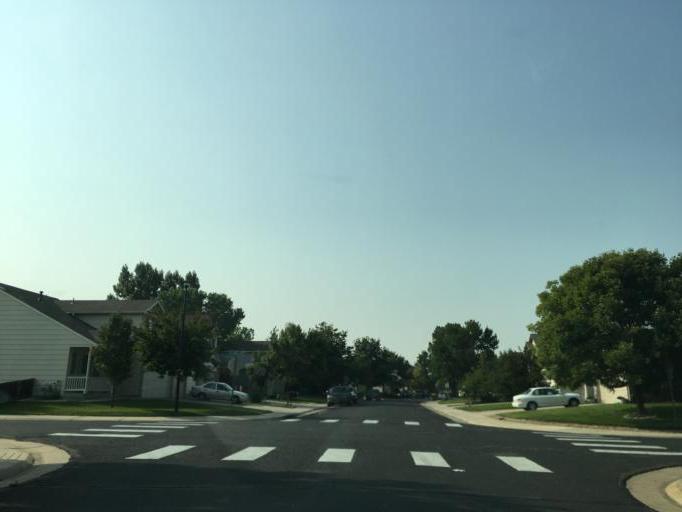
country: US
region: Colorado
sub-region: Adams County
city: Todd Creek
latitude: 39.9064
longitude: -104.8535
